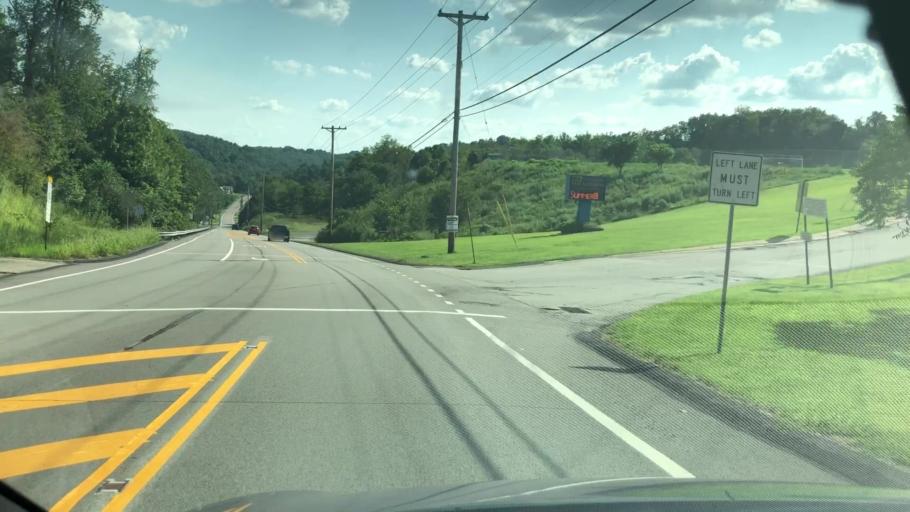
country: US
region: Pennsylvania
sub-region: Allegheny County
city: East McKeesport
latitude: 40.3651
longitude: -79.7846
